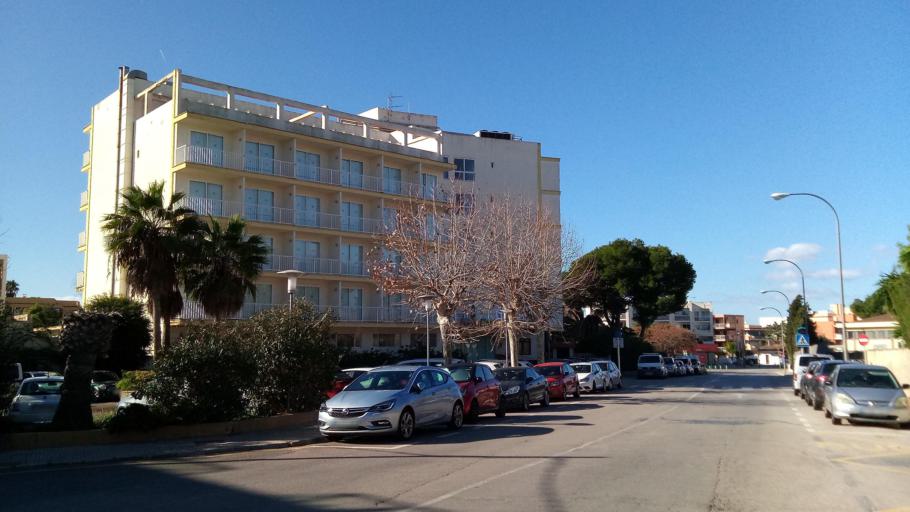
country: ES
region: Balearic Islands
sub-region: Illes Balears
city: s'Arenal
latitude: 39.5381
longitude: 2.7172
